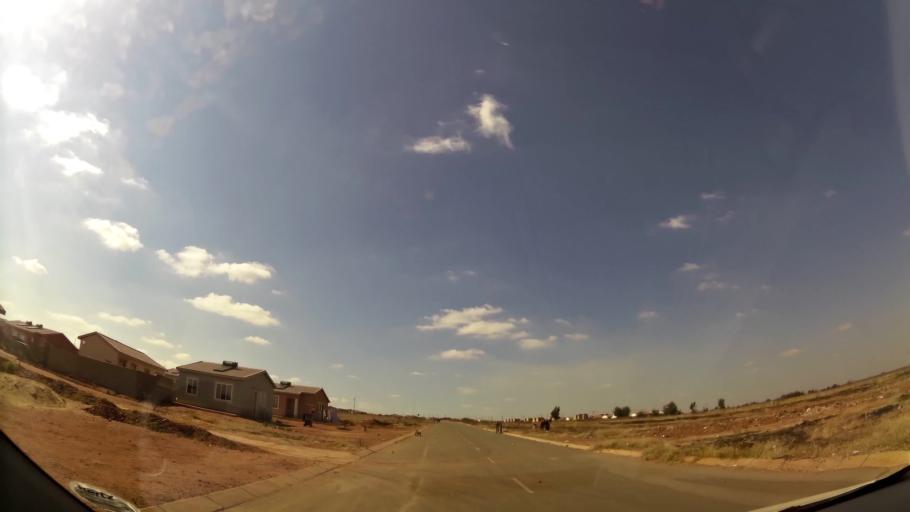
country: ZA
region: Gauteng
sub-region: West Rand District Municipality
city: Randfontein
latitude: -26.1712
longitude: 27.7699
